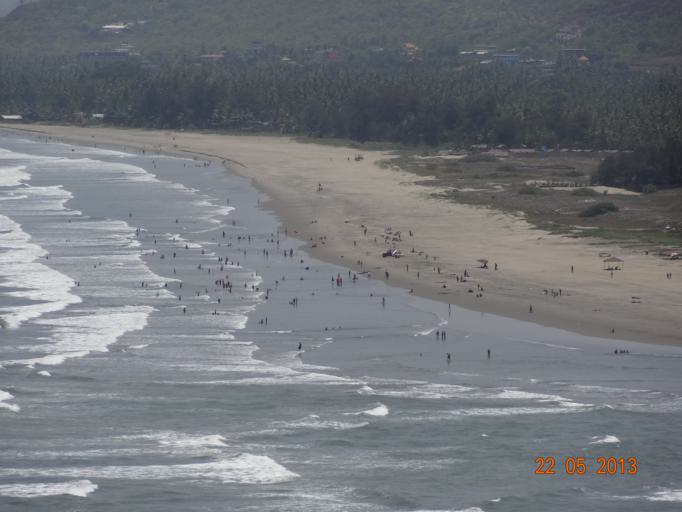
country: IN
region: Goa
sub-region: North Goa
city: Vagator
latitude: 15.6068
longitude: 73.7358
